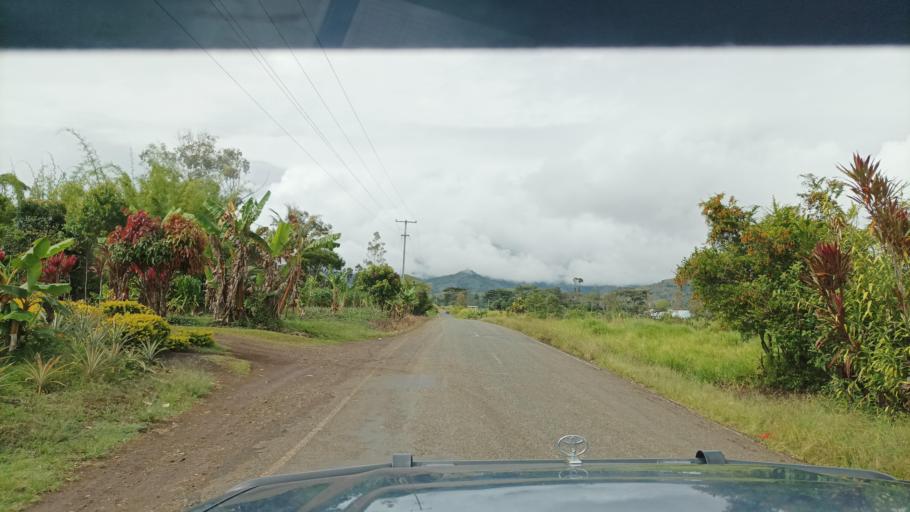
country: PG
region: Jiwaka
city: Minj
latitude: -5.8919
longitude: 144.6817
